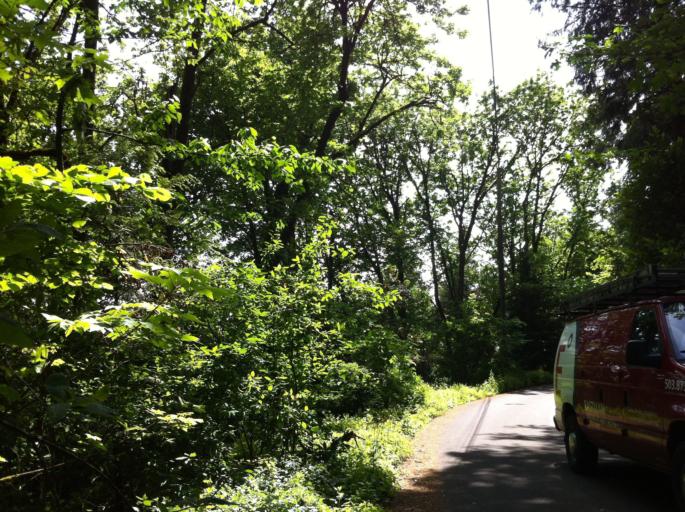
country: US
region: Oregon
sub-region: Washington County
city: Raleigh Hills
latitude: 45.4890
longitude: -122.7494
